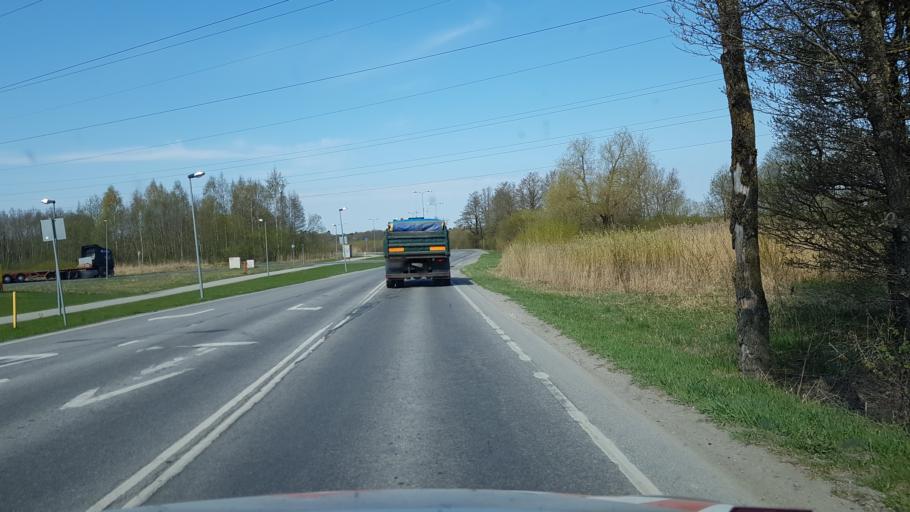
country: EE
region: Harju
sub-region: Saue vald
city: Laagri
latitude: 59.4074
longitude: 24.6188
